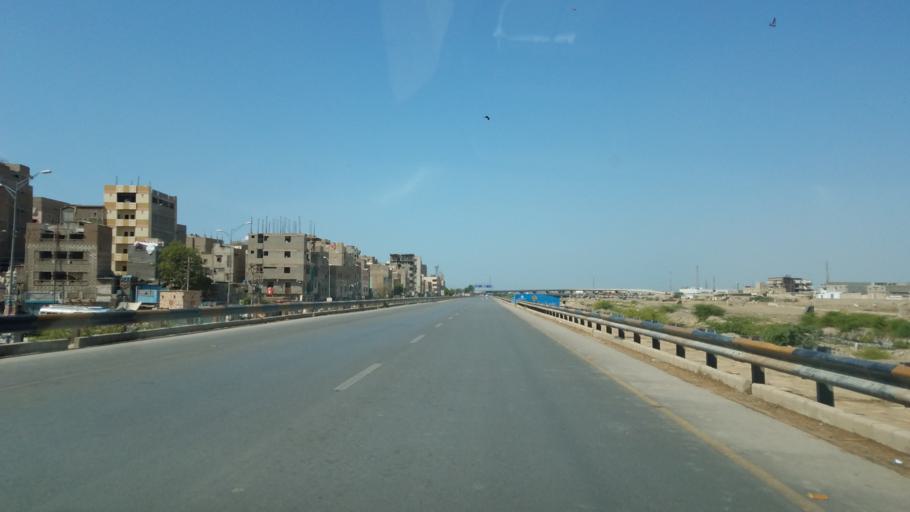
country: PK
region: Sindh
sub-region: Karachi District
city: Karachi
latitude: 24.8748
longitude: 66.9839
